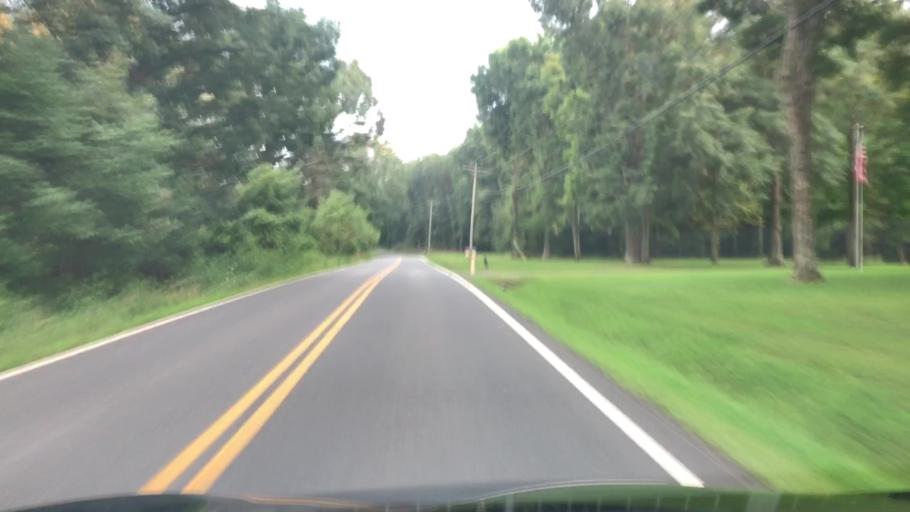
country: US
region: Virginia
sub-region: Fauquier County
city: Bealeton
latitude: 38.5447
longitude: -77.6767
